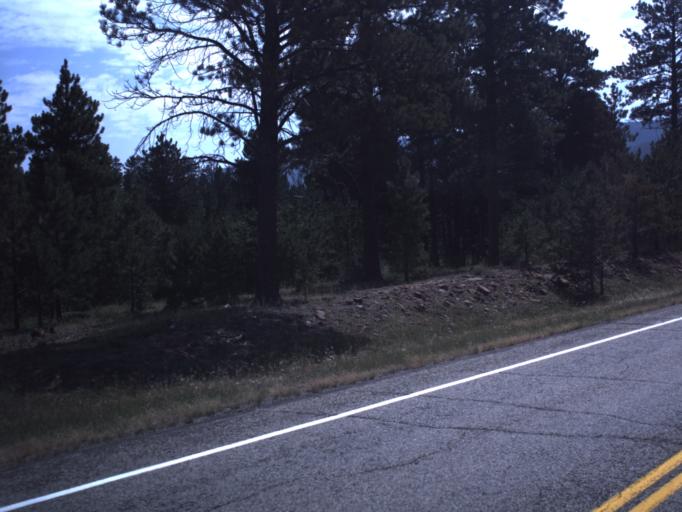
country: US
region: Utah
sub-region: Daggett County
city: Manila
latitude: 40.8507
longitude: -109.5884
